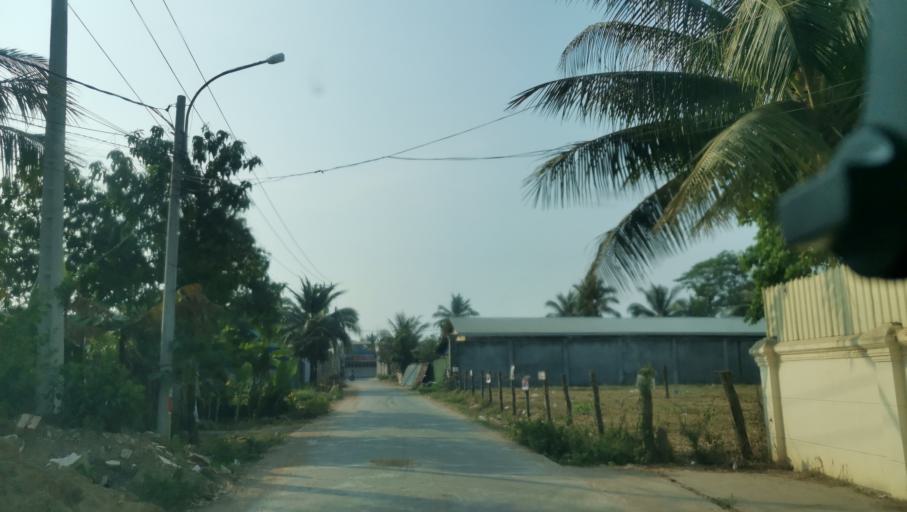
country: KH
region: Battambang
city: Battambang
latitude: 13.0857
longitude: 103.1930
